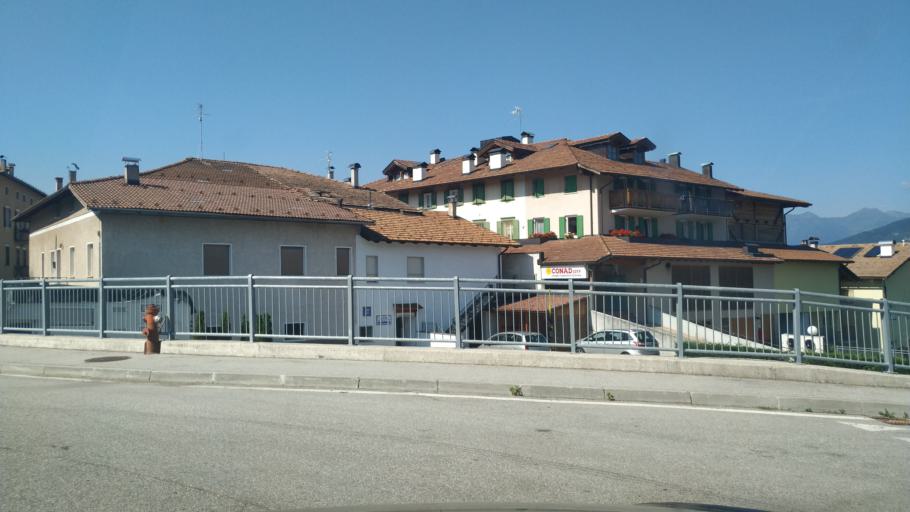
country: IT
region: Trentino-Alto Adige
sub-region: Provincia di Trento
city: Cavareno
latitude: 46.4112
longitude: 11.1386
